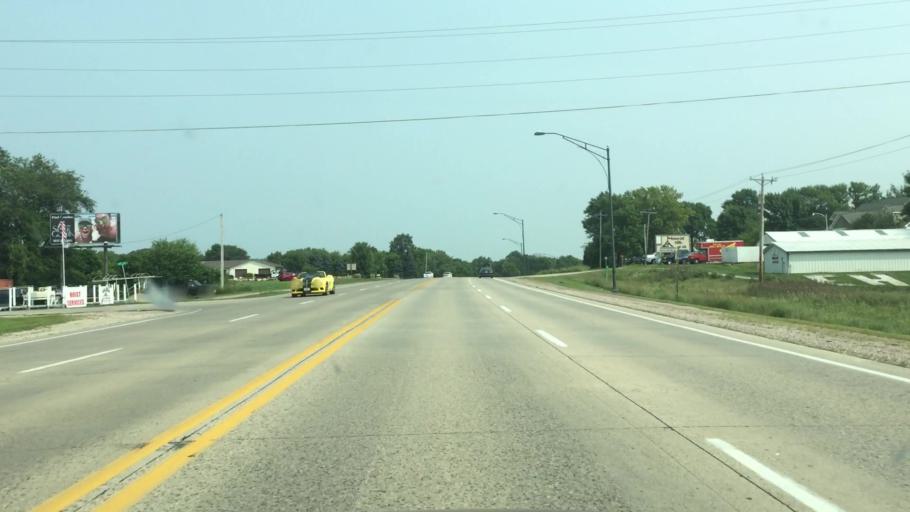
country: US
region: Iowa
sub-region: Dickinson County
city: Arnolds Park
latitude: 43.3567
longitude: -95.1420
